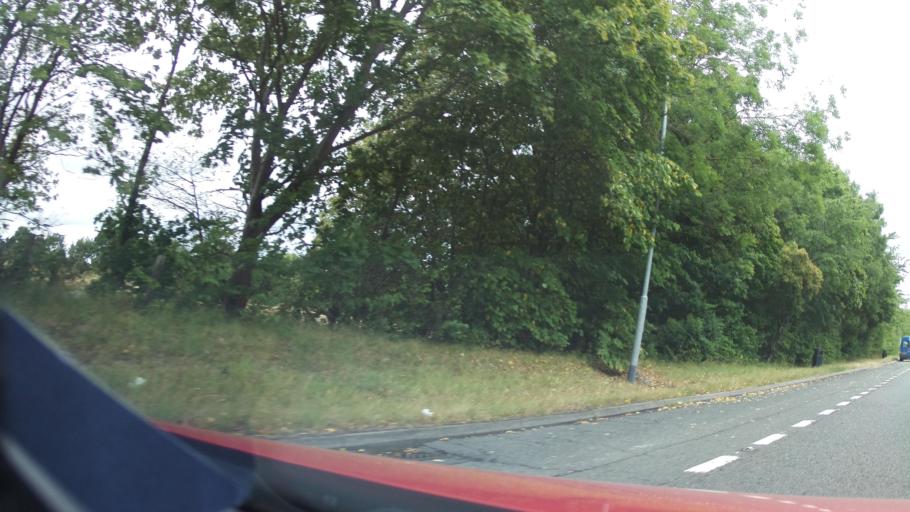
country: GB
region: England
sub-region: Nottinghamshire
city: Eastwood
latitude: 53.0121
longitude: -1.3152
